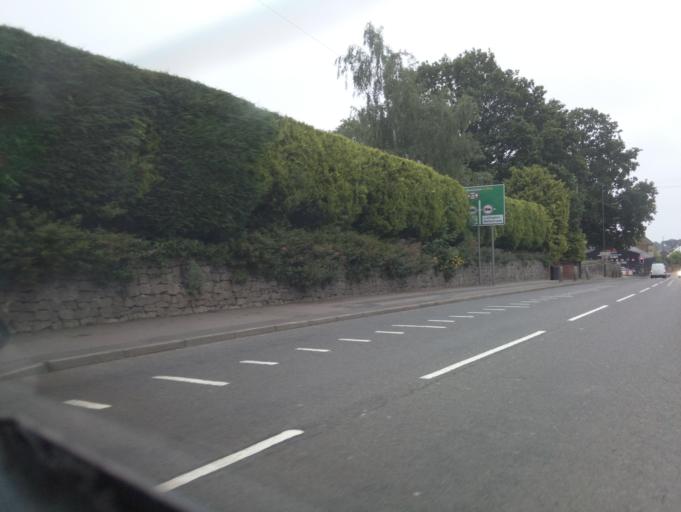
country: GB
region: England
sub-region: Derbyshire
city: Netherseal
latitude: 52.7364
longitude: -1.5658
